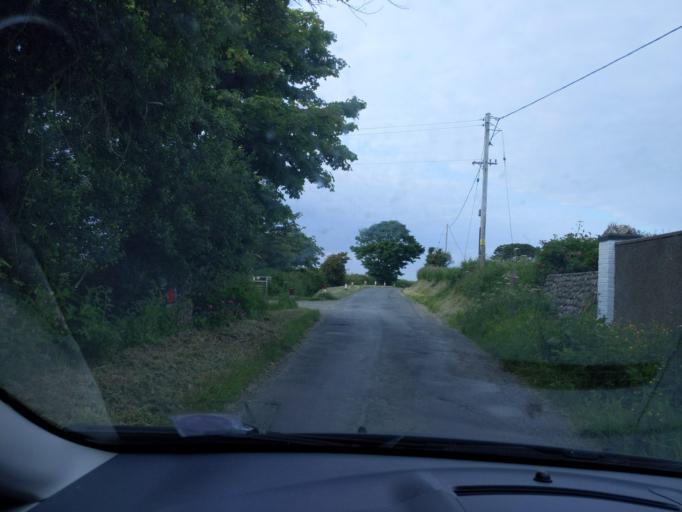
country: IM
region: Ramsey
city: Ramsey
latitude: 54.3903
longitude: -4.4475
